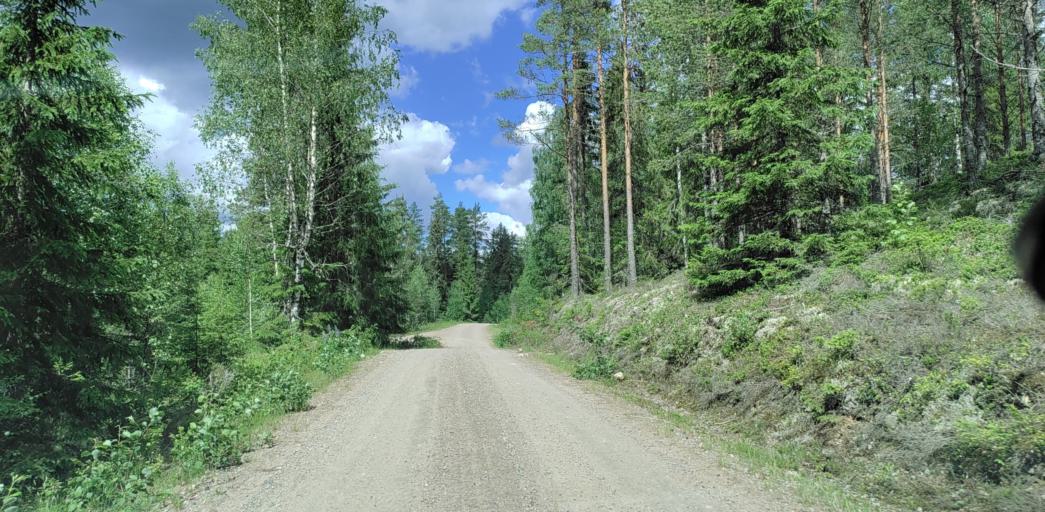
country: SE
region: Vaermland
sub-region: Hagfors Kommun
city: Ekshaerad
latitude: 60.0769
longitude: 13.2917
